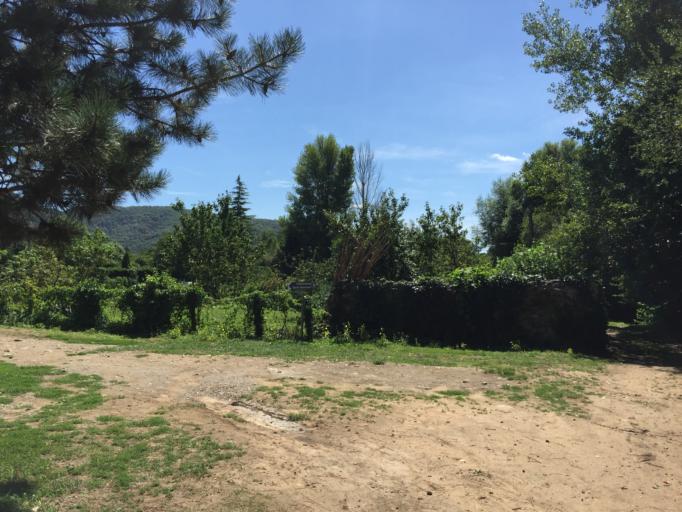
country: FR
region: Midi-Pyrenees
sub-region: Departement de l'Aveyron
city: Villefranche-de-Rouergue
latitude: 44.3454
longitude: 2.0293
